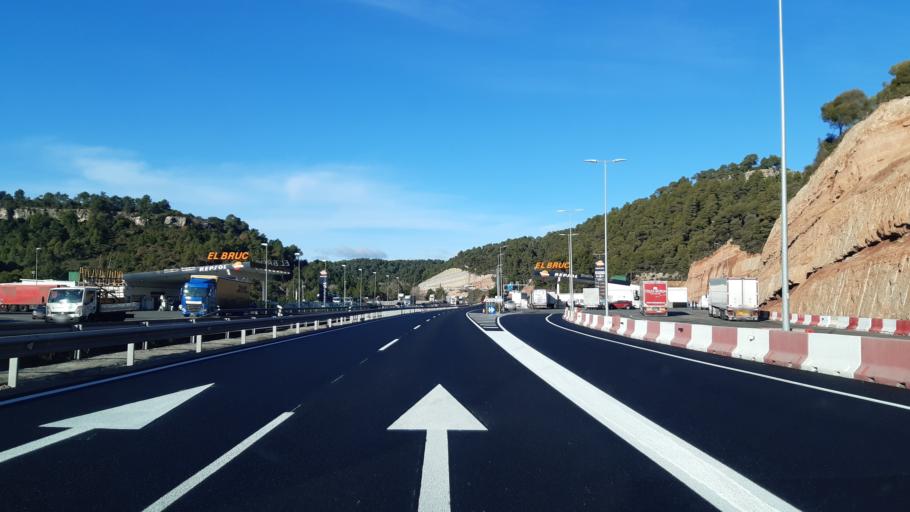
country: ES
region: Catalonia
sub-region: Provincia de Barcelona
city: Castelloli
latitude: 41.5929
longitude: 1.7523
